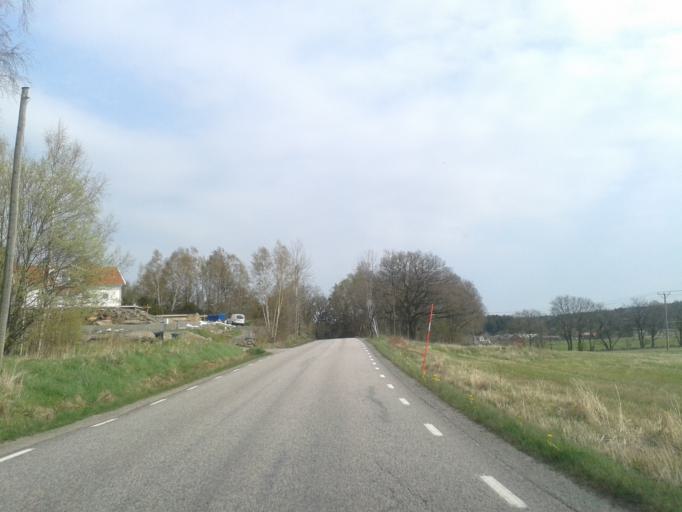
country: SE
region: Vaestra Goetaland
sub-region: Kungalvs Kommun
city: Kode
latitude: 57.9100
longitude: 11.8014
